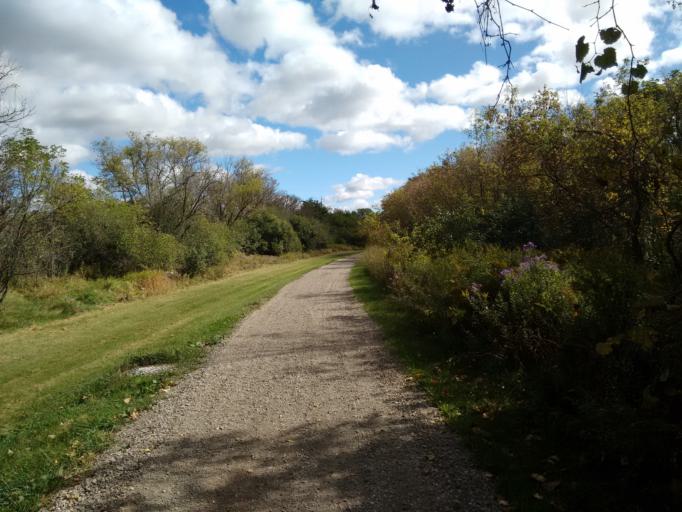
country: CA
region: Ontario
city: Stratford
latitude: 43.2473
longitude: -81.1431
